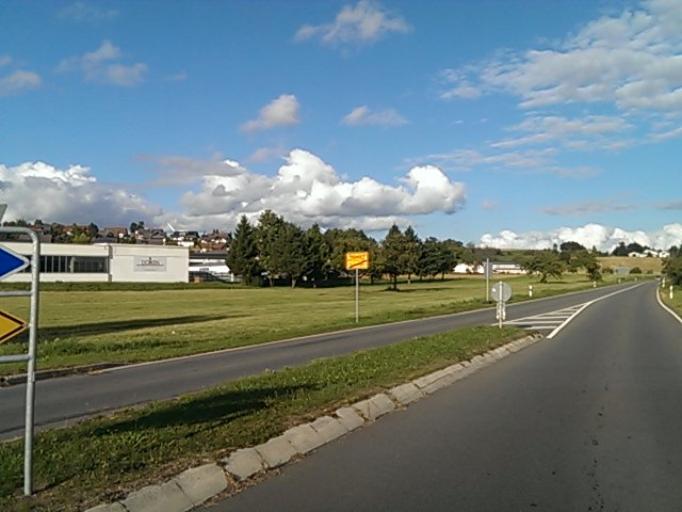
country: DE
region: Baden-Wuerttemberg
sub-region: Freiburg Region
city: Dunningen
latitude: 48.2080
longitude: 8.5131
